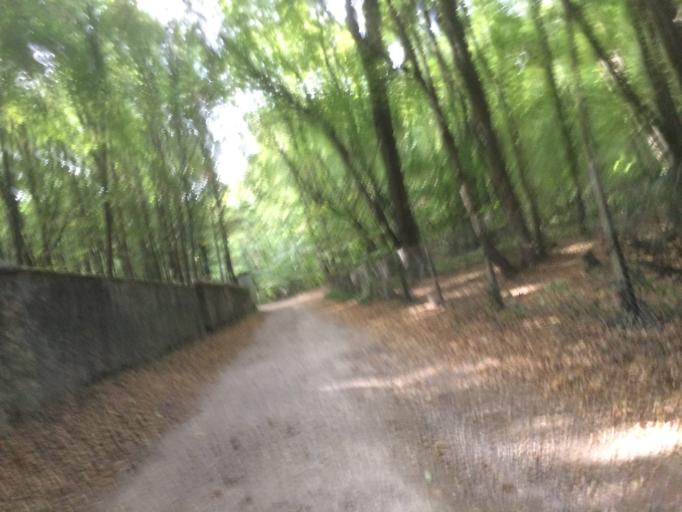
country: FR
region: Ile-de-France
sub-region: Departement des Yvelines
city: Bonnelles
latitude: 48.6162
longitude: 2.0152
